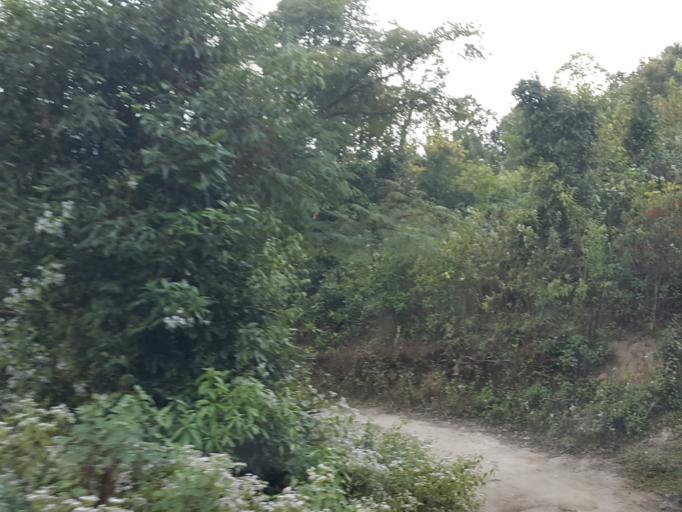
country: TH
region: Chiang Mai
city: Om Koi
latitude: 17.7814
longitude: 98.3012
